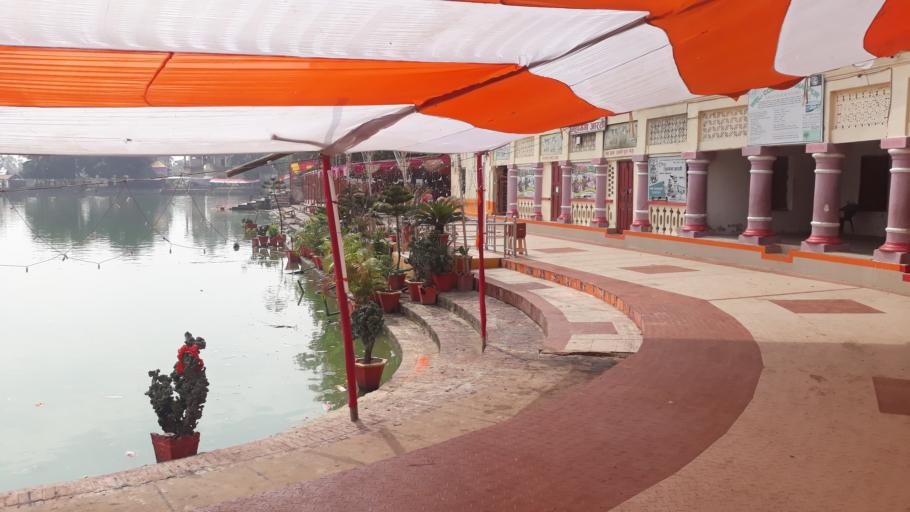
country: NP
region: Central Region
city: Janakpur
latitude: 26.7293
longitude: 85.9297
